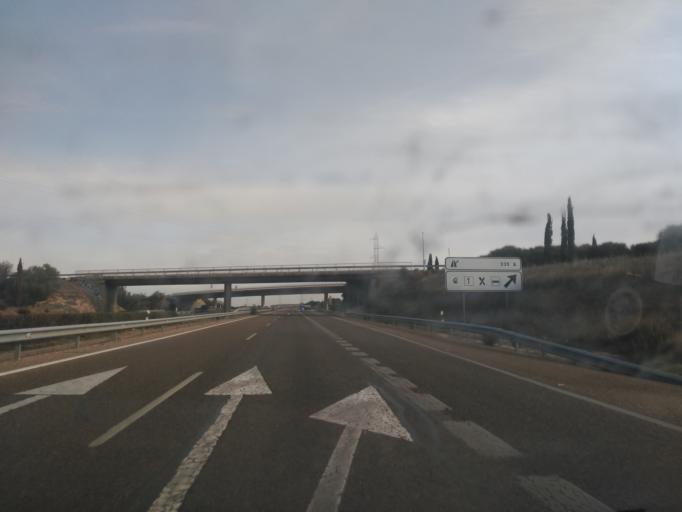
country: ES
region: Castille and Leon
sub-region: Provincia de Salamanca
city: Villares de la Reina
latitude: 41.0000
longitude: -5.6296
